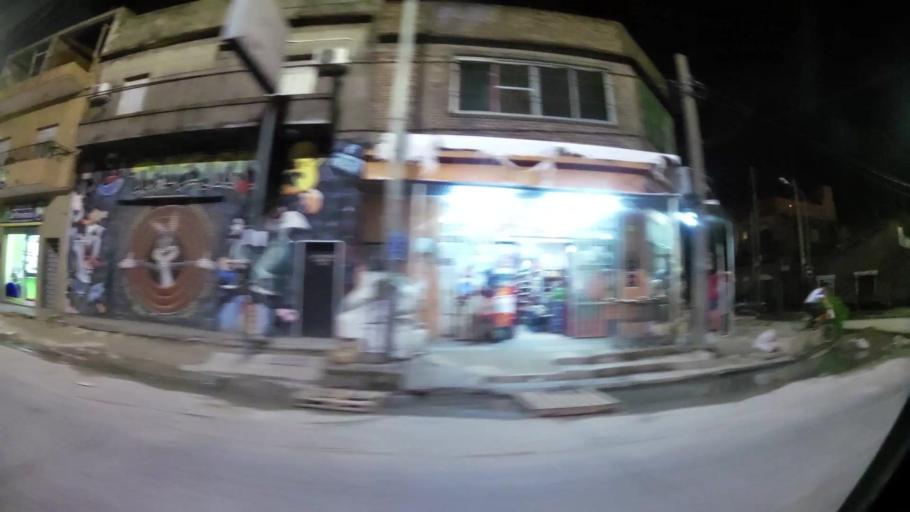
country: AR
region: Buenos Aires
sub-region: Partido de Lanus
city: Lanus
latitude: -34.7188
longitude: -58.3587
